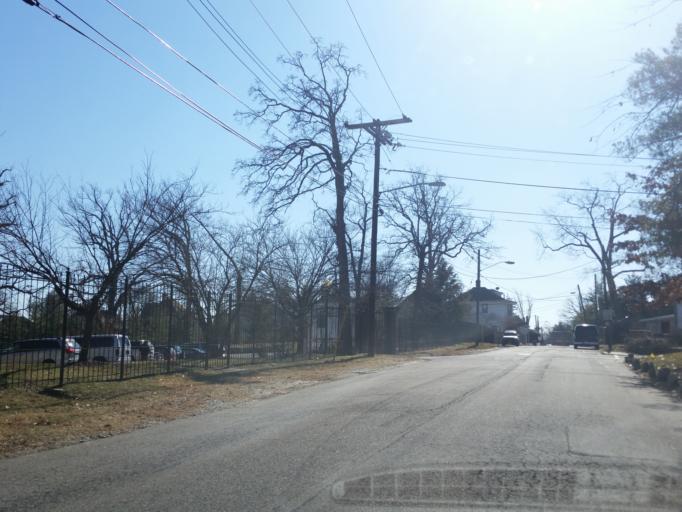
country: US
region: Maryland
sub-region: Montgomery County
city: Takoma Park
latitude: 38.9511
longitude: -77.0348
